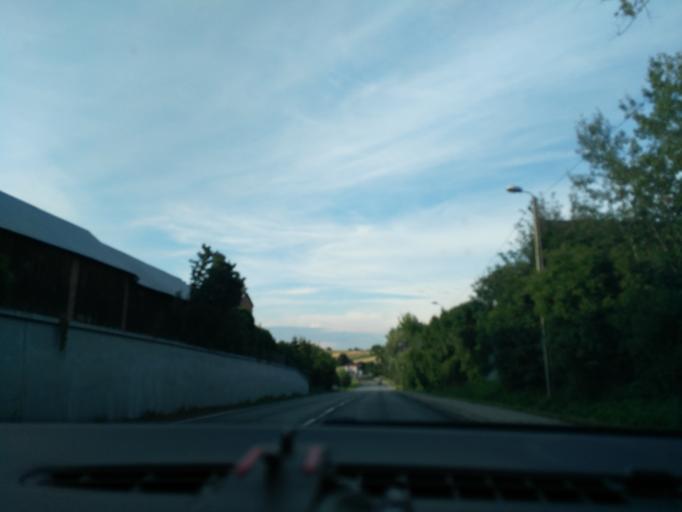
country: PL
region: Lublin Voivodeship
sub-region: Powiat krasnicki
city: Krasnik
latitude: 50.9010
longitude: 22.2710
